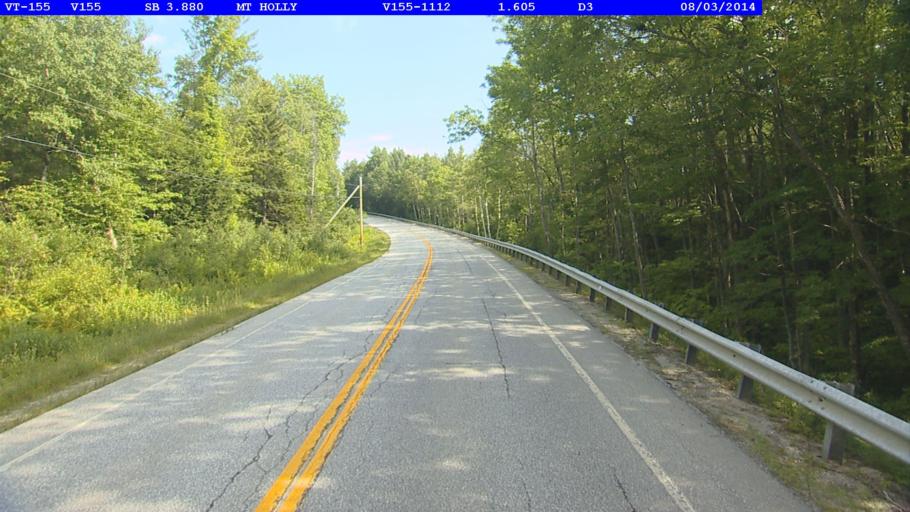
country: US
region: Vermont
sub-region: Windsor County
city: Chester
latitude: 43.3844
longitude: -72.8020
